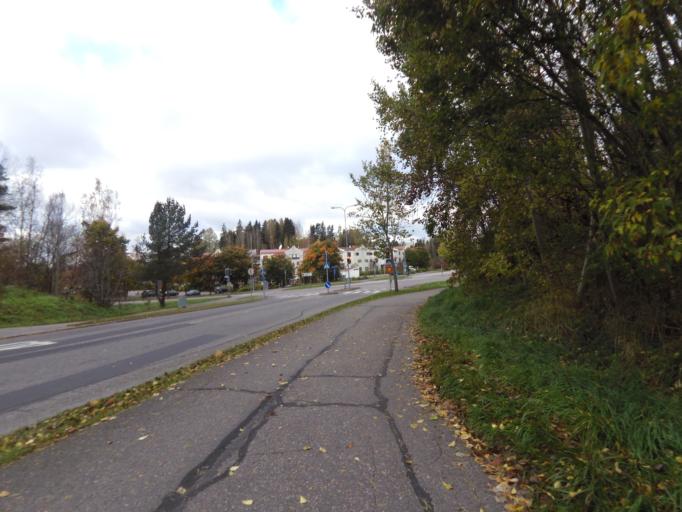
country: FI
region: Uusimaa
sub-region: Helsinki
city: Espoo
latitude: 60.1969
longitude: 24.6704
